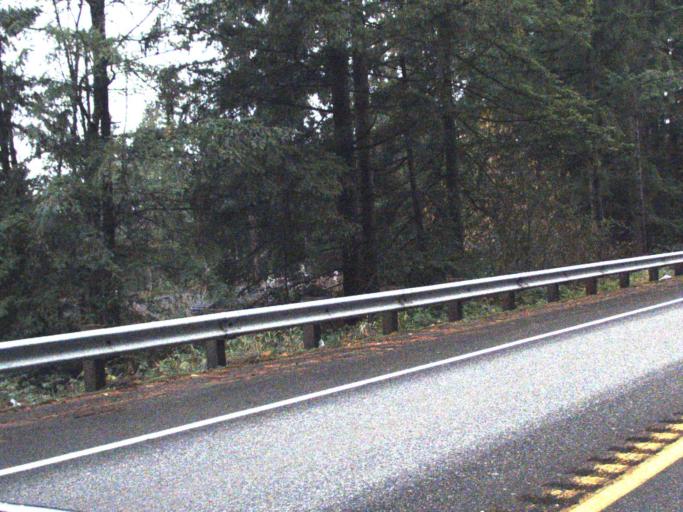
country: US
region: Washington
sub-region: Snohomish County
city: Fobes Hill
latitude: 47.9657
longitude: -122.1021
